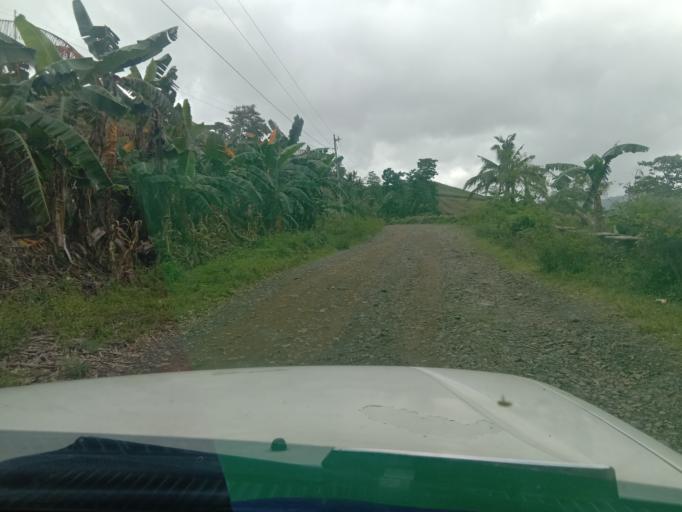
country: PH
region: Western Visayas
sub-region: Province of Capiz
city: Lantangan
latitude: 11.3723
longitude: 122.8870
